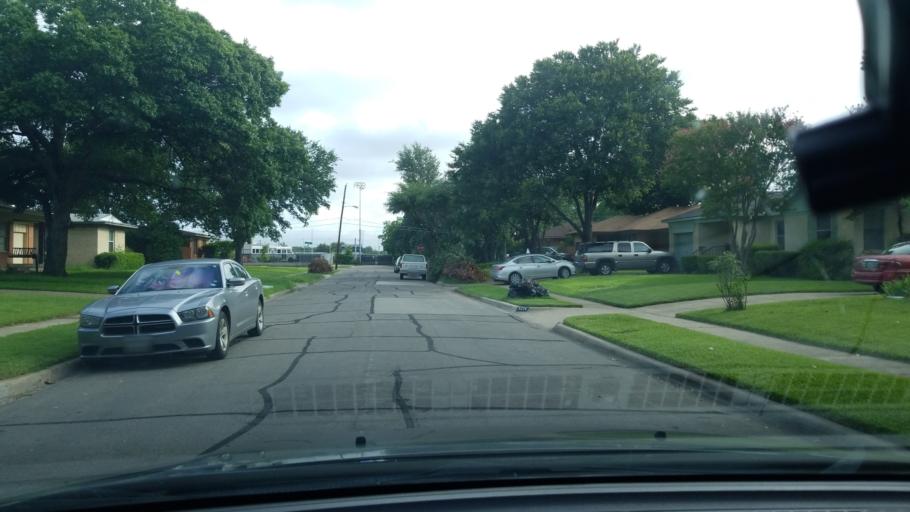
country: US
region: Texas
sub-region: Dallas County
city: Mesquite
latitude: 32.8167
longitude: -96.6787
